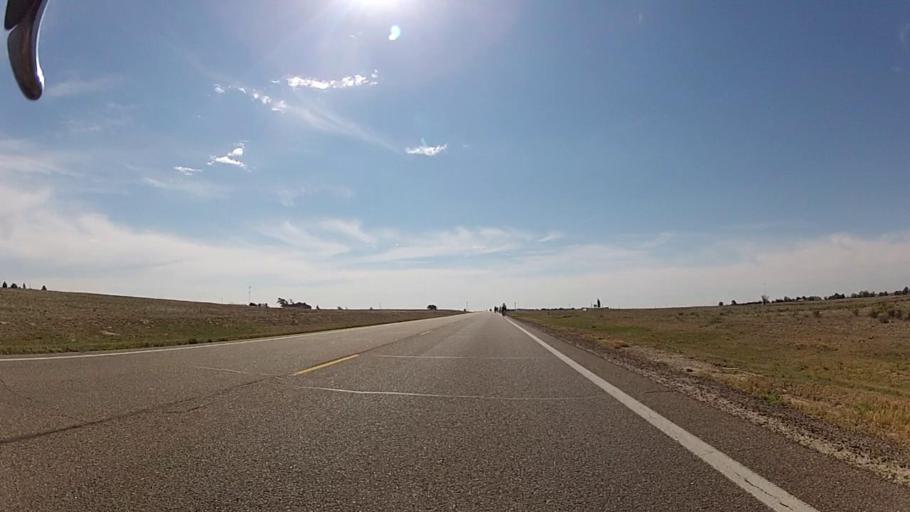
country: US
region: Kansas
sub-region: Grant County
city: Ulysses
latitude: 37.5679
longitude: -101.3219
